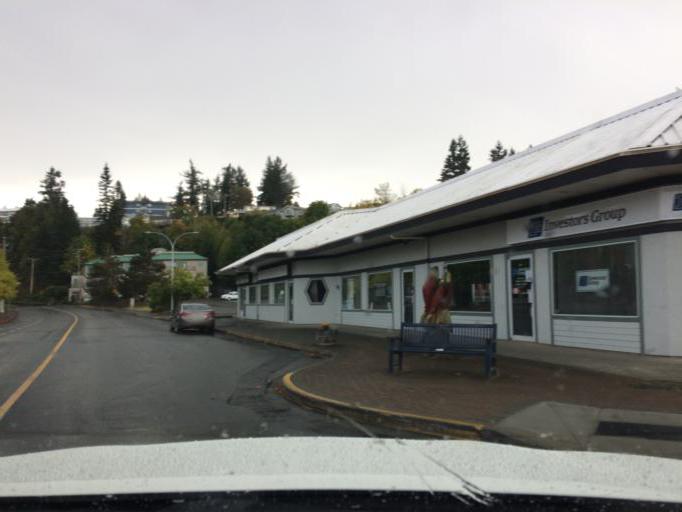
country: CA
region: British Columbia
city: Campbell River
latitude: 50.0263
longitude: -125.2470
